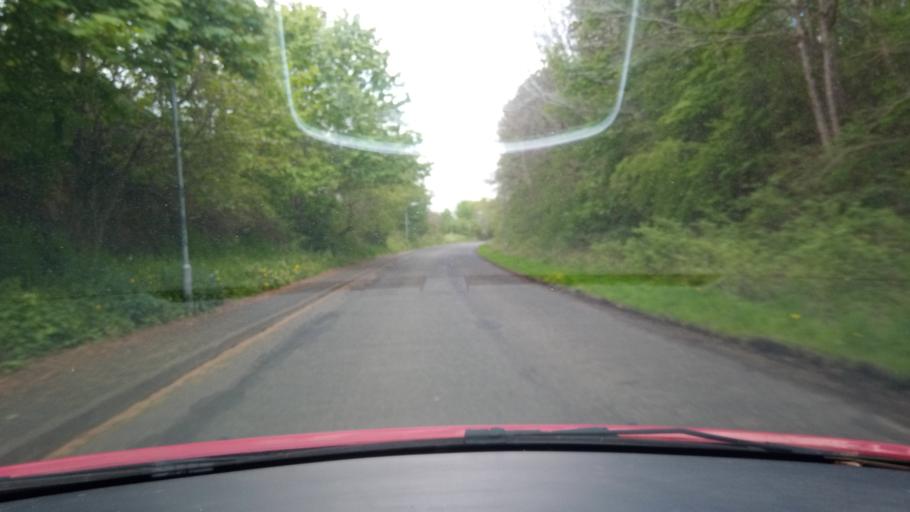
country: GB
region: Scotland
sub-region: The Scottish Borders
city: Melrose
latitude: 55.5980
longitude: -2.7097
